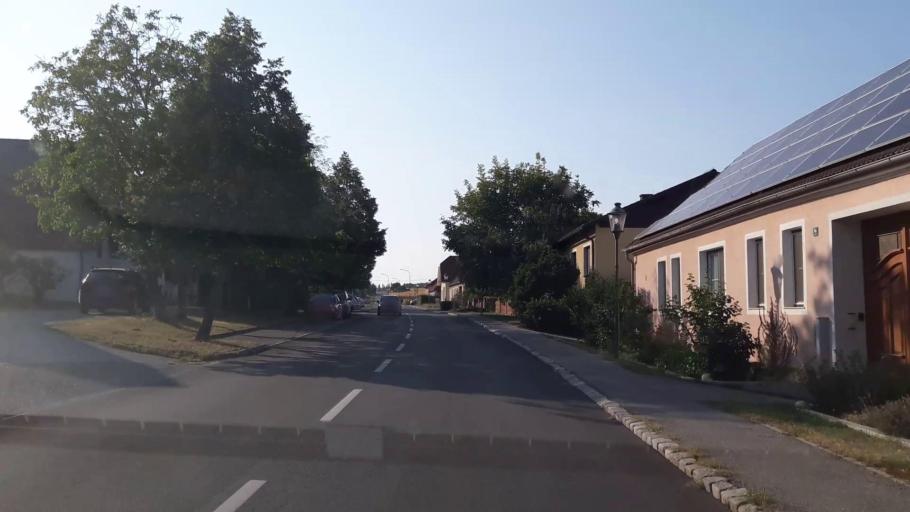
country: AT
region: Lower Austria
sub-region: Politischer Bezirk Ganserndorf
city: Orth an der Donau
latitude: 48.0682
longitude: 16.7036
